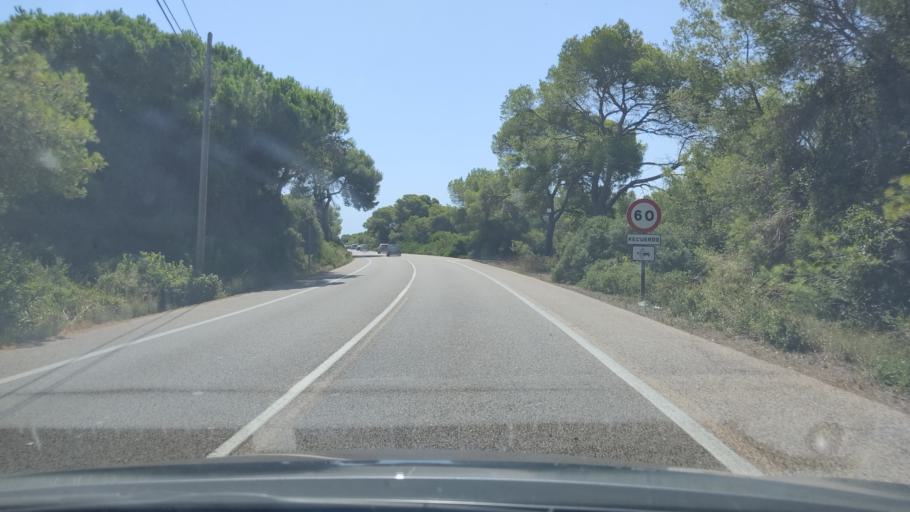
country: ES
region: Valencia
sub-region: Provincia de Valencia
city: Sollana
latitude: 39.3160
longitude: -0.3045
